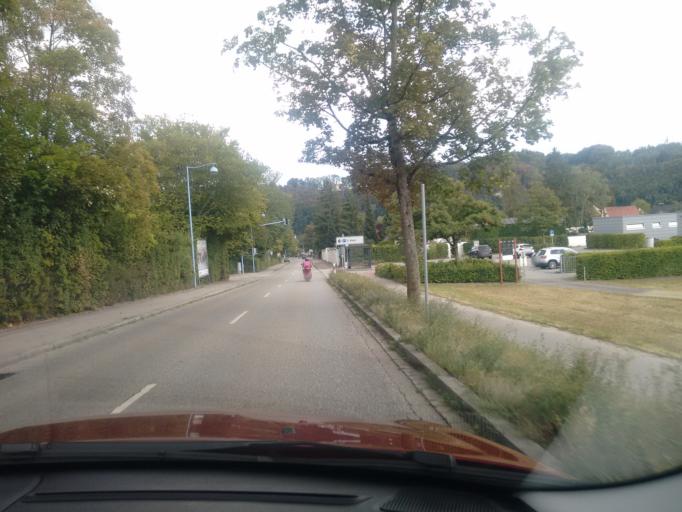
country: DE
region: Bavaria
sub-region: Upper Bavaria
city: Burghausen
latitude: 48.1555
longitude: 12.8204
